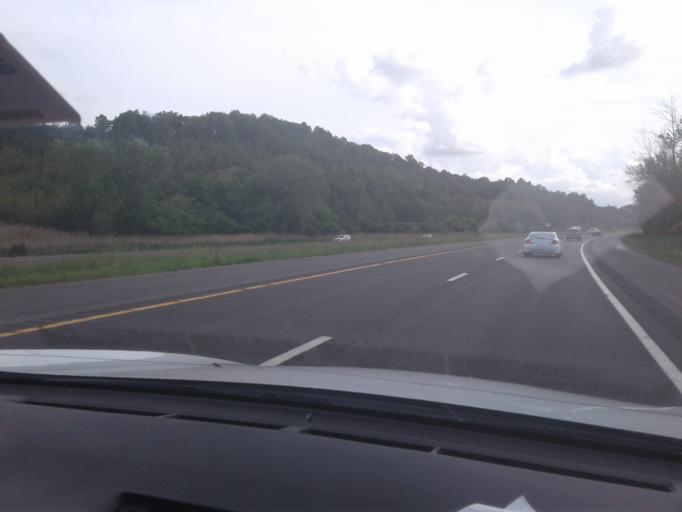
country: US
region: New York
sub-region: Onondaga County
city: East Syracuse
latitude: 43.0186
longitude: -76.0646
